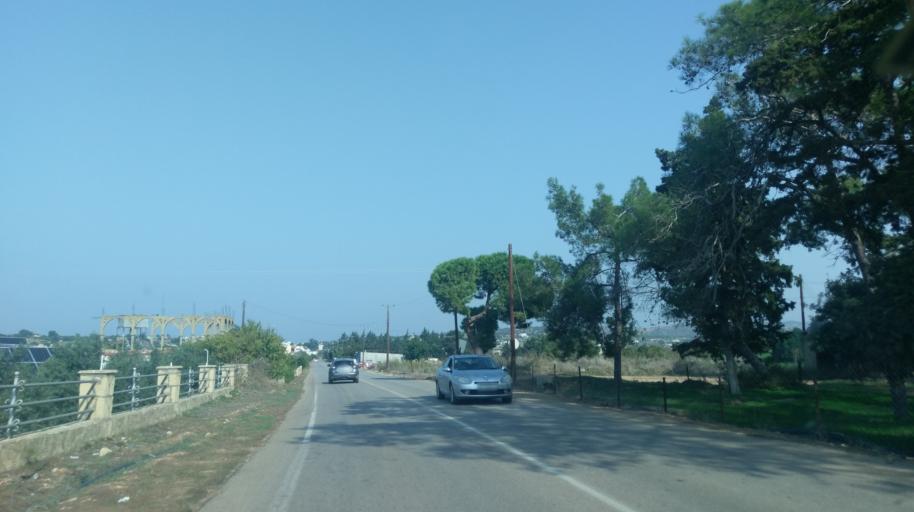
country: CY
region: Ammochostos
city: Leonarisso
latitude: 35.4934
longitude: 34.1569
